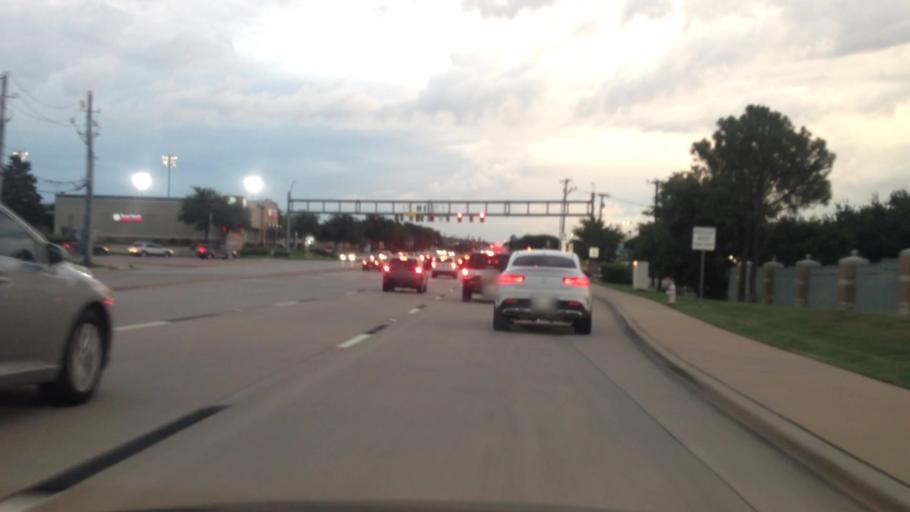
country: US
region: Texas
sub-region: Tarrant County
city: Hurst
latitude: 32.8544
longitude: -97.1861
